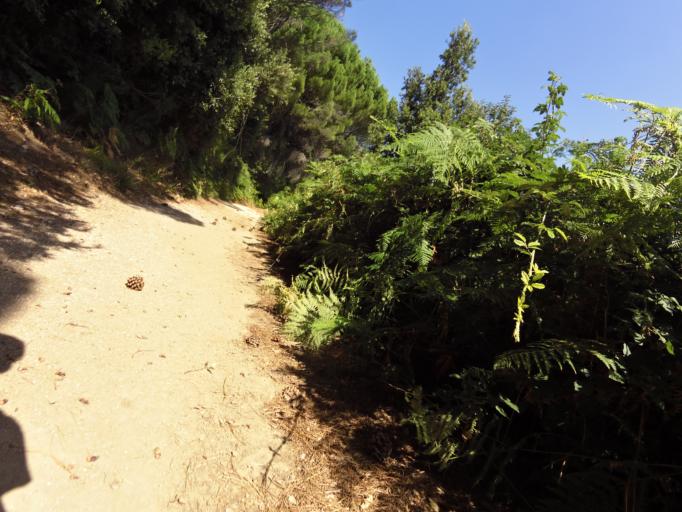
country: IT
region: Calabria
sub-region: Provincia di Reggio Calabria
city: Bivongi
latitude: 38.5091
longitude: 16.4353
